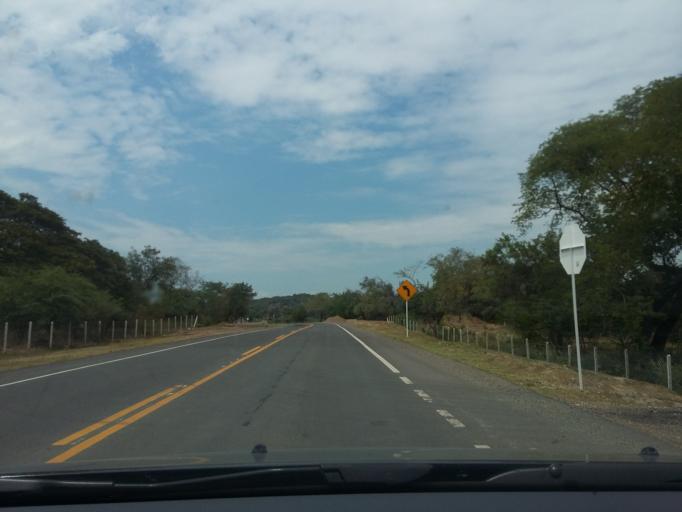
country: CO
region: Tolima
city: Ambalema
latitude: 4.8659
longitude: -74.7393
